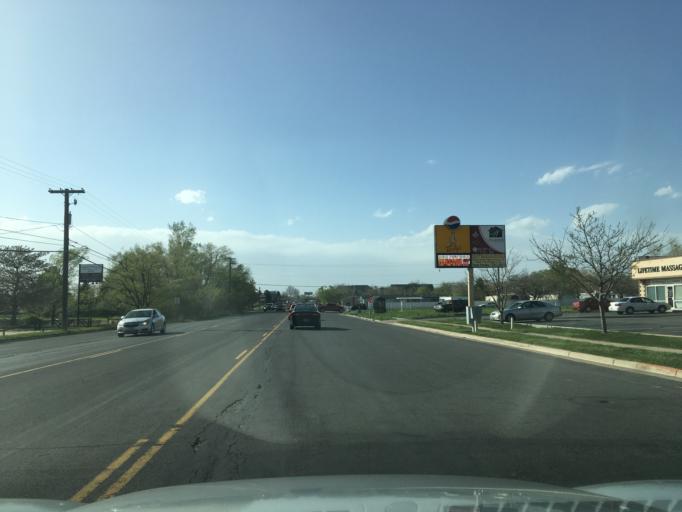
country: US
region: Utah
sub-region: Davis County
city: Kaysville
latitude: 41.0445
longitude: -111.9503
